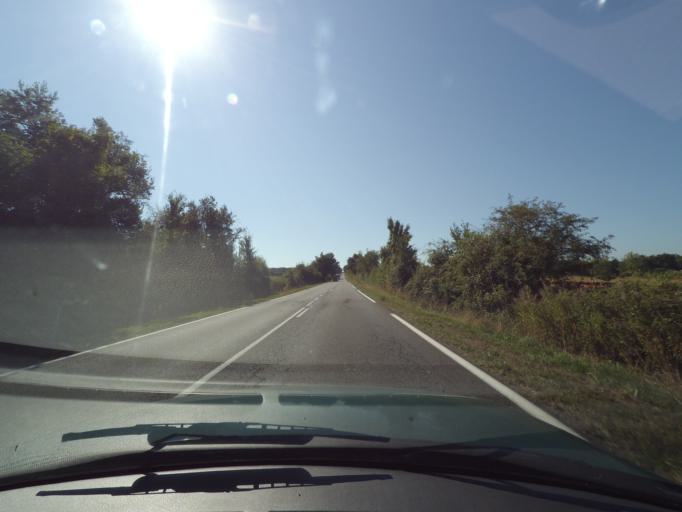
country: FR
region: Poitou-Charentes
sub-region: Departement de la Vienne
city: Lussac-les-Chateaux
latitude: 46.3644
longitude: 0.7711
